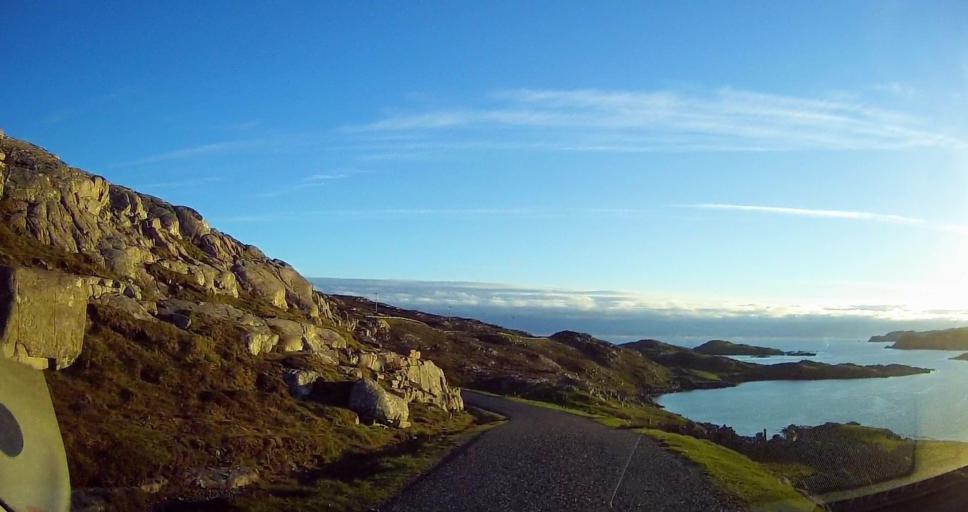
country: GB
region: Scotland
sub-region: Shetland Islands
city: Lerwick
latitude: 60.4466
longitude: -1.4325
